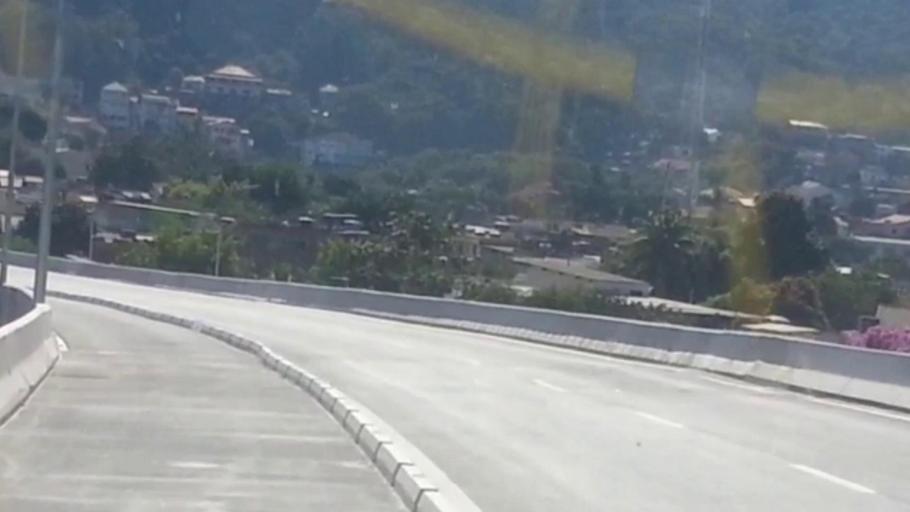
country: BR
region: Rio de Janeiro
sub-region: Nilopolis
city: Nilopolis
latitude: -22.9186
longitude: -43.3963
